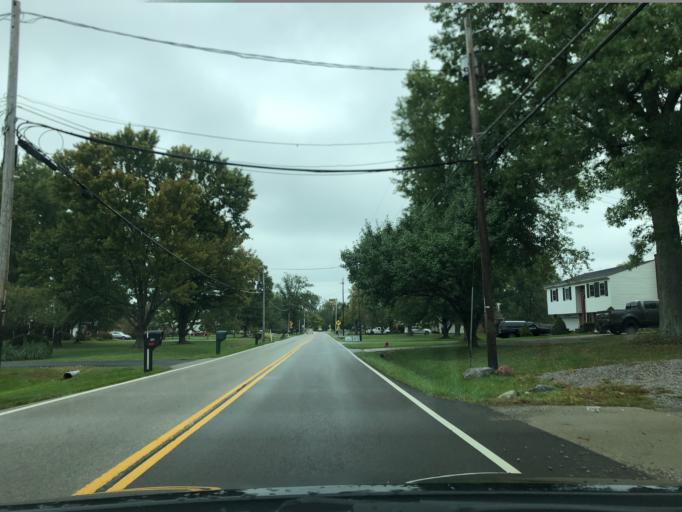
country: US
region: Ohio
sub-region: Hamilton County
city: Loveland
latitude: 39.2382
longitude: -84.2640
